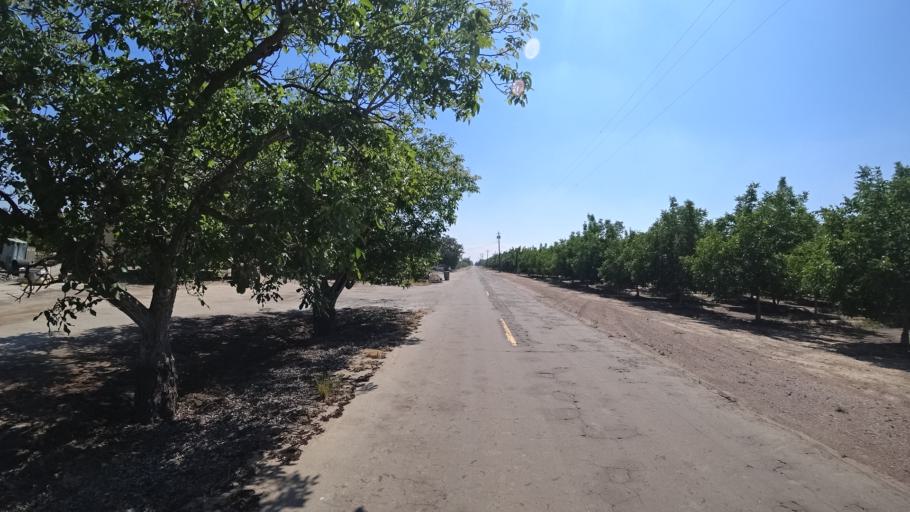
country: US
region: California
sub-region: Fresno County
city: Kingsburg
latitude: 36.4741
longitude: -119.5697
